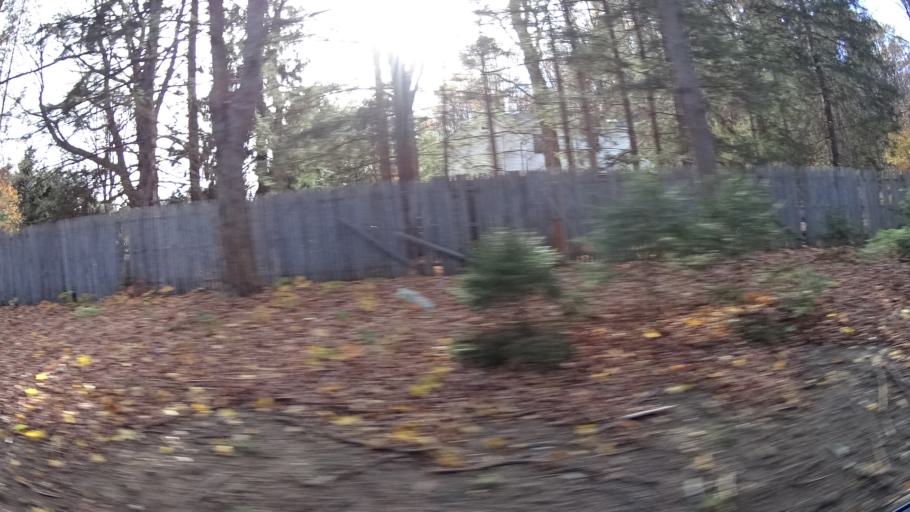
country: US
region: New Jersey
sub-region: Morris County
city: Mendham
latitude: 40.7700
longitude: -74.5661
